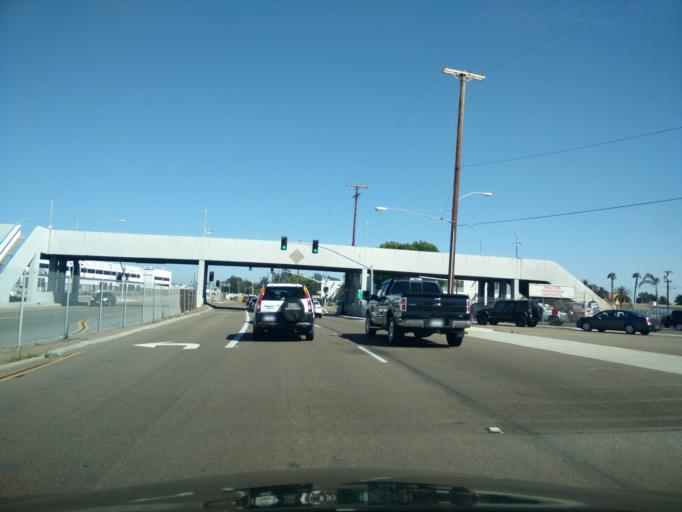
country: US
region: California
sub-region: San Diego County
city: San Diego
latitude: 32.7476
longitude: -117.1984
